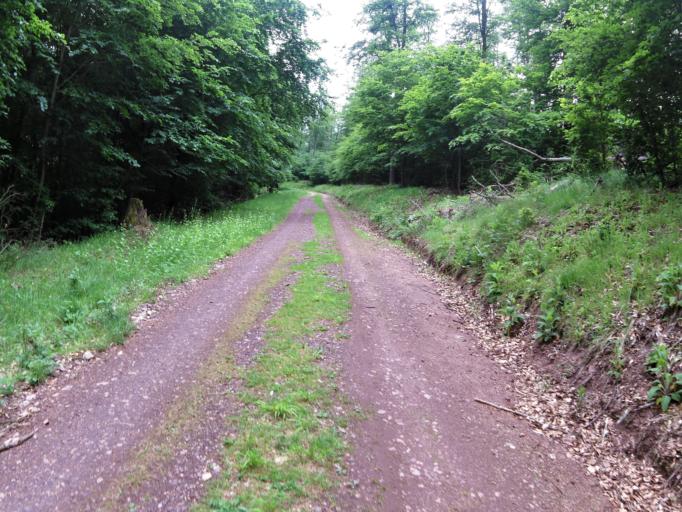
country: DE
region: Thuringia
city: Eisenach
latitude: 50.9462
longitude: 10.3170
